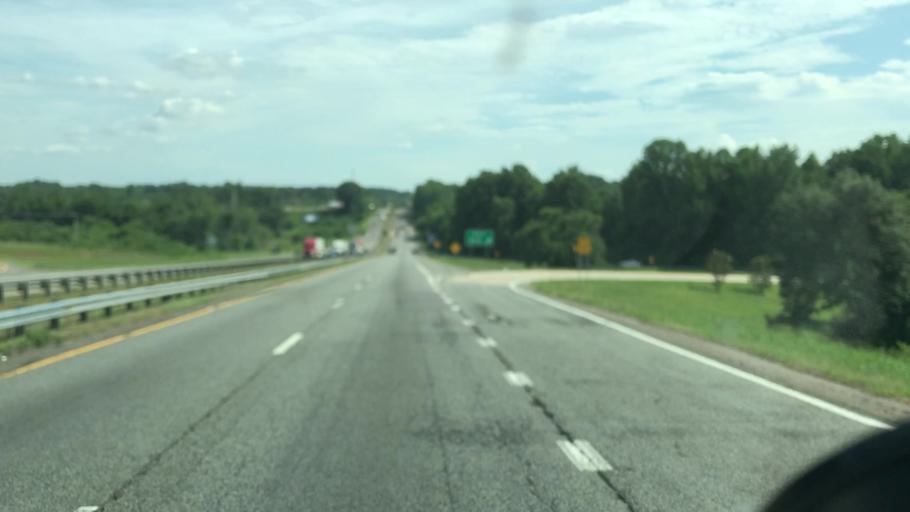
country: US
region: North Carolina
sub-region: Iredell County
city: Statesville
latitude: 35.8092
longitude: -80.8613
